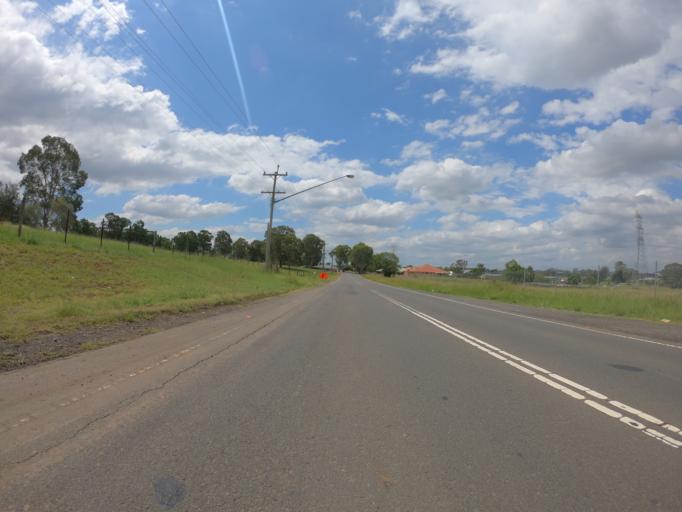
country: AU
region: New South Wales
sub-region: Penrith Municipality
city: Kingswood Park
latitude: -33.8244
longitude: 150.7606
